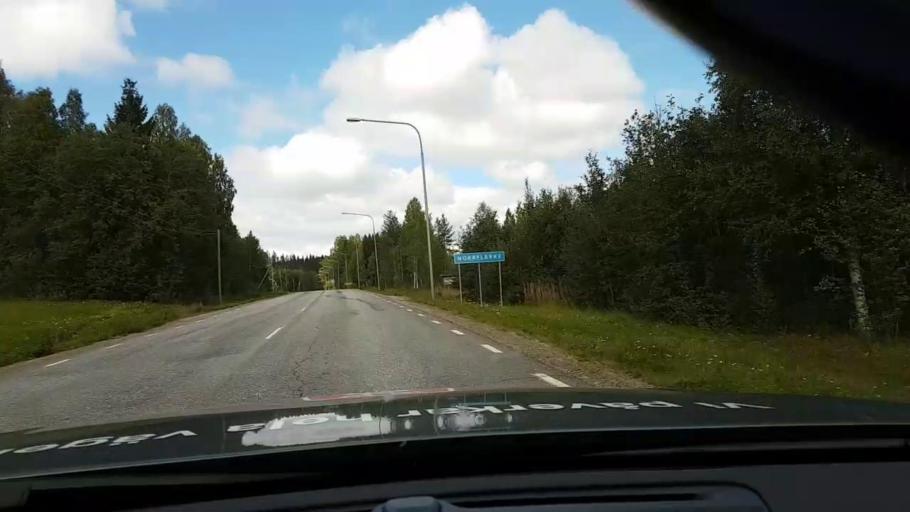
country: SE
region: Vaesternorrland
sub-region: OErnskoeldsviks Kommun
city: Bredbyn
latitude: 63.4881
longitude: 18.0843
